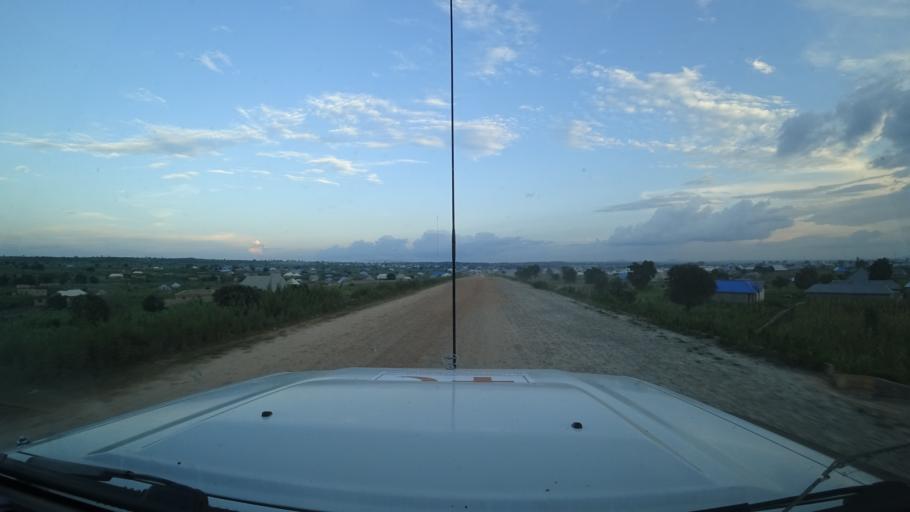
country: NG
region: Niger
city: Minna
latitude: 9.6513
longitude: 6.5780
